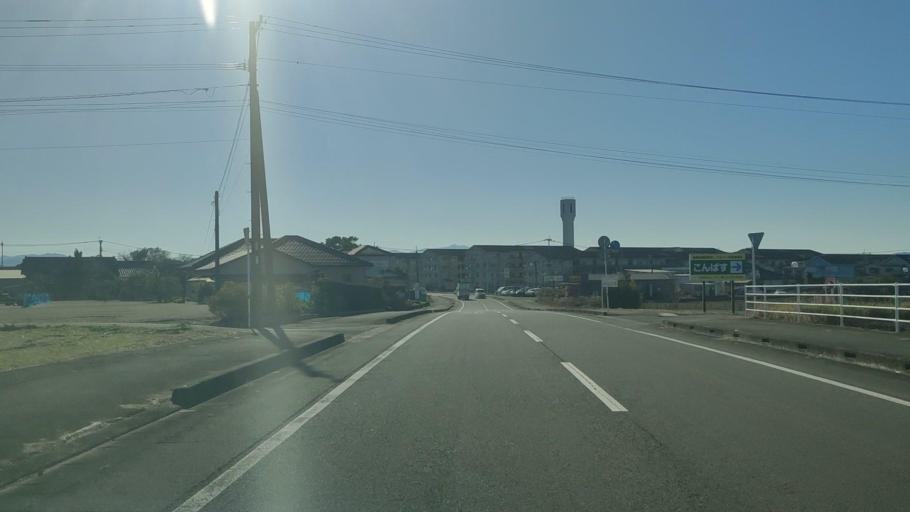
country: JP
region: Miyazaki
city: Miyazaki-shi
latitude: 31.9544
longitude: 131.4620
